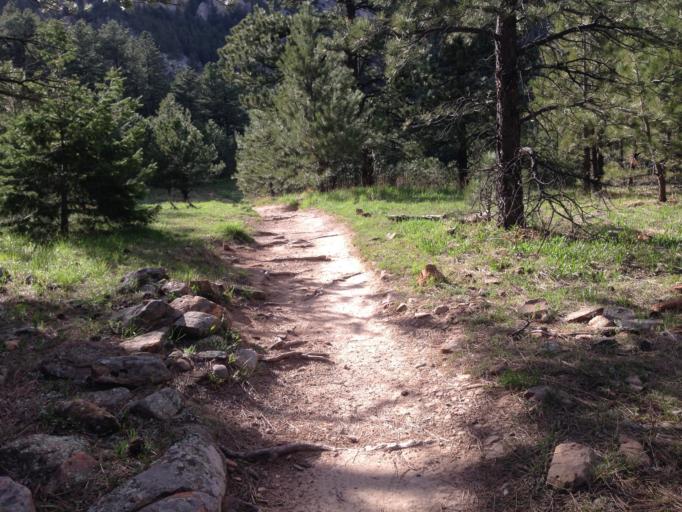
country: US
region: Colorado
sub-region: Boulder County
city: Boulder
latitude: 39.9492
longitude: -105.2792
